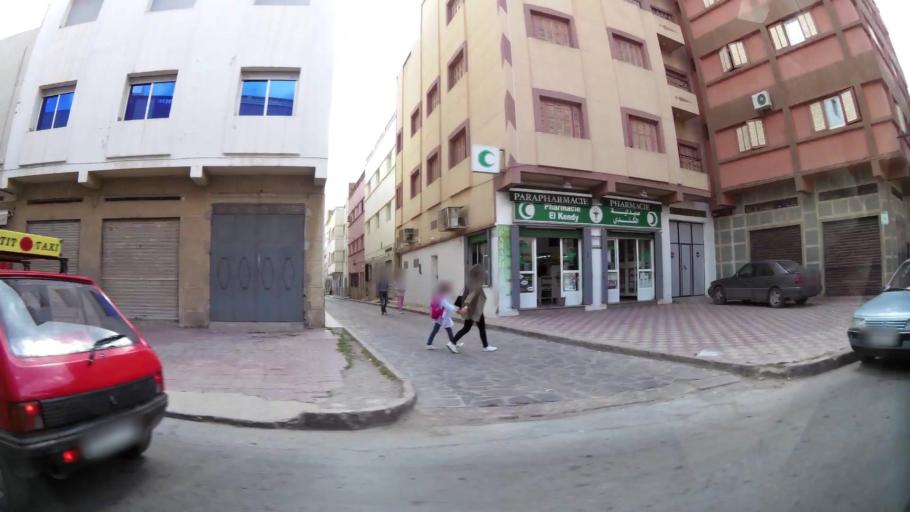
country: MA
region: Oriental
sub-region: Nador
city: Nador
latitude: 35.1703
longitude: -2.9299
